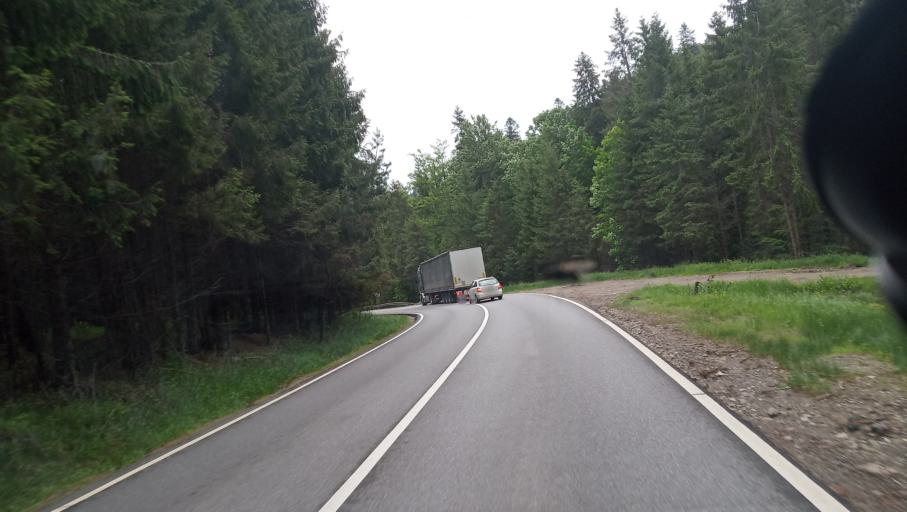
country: RO
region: Neamt
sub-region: Comuna Pipirig
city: Dolhesti
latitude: 47.1863
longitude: 26.0247
